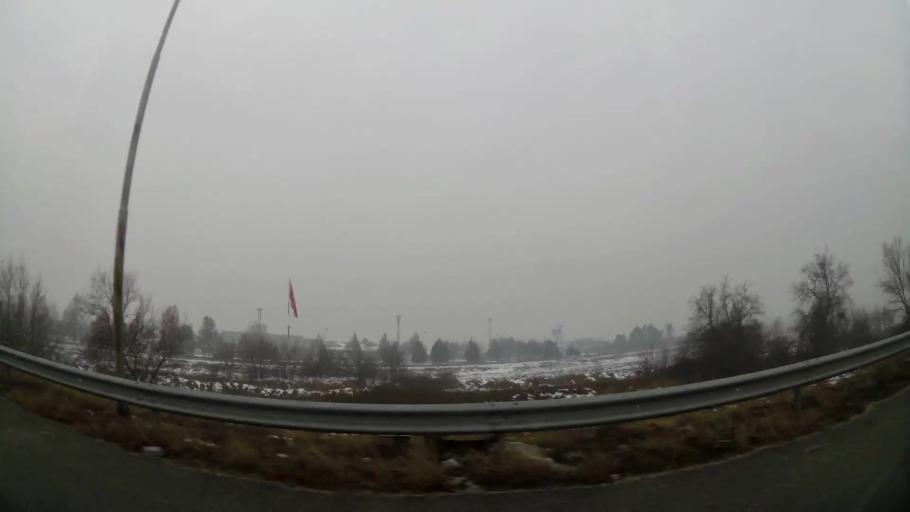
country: MK
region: Petrovec
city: Petrovec
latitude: 41.9569
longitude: 21.6310
